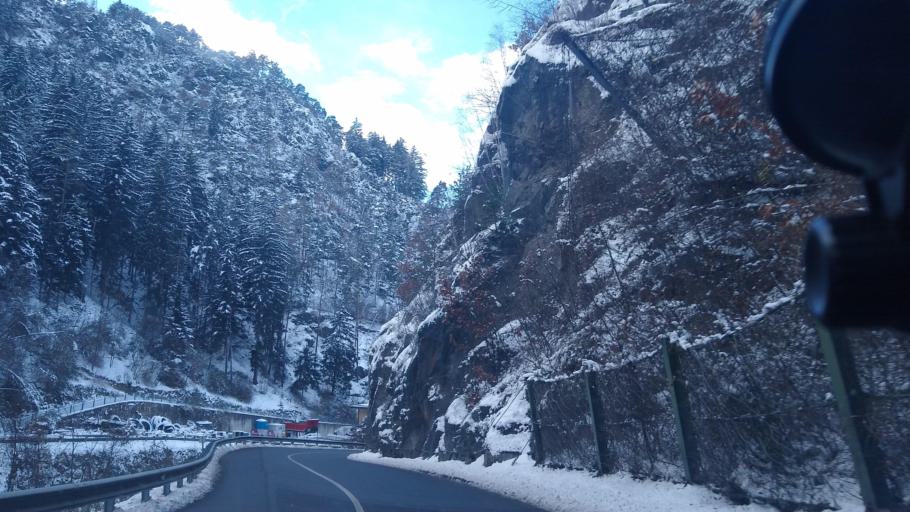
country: IT
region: Trentino-Alto Adige
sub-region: Bolzano
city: Velturno
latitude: 46.6534
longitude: 11.6000
